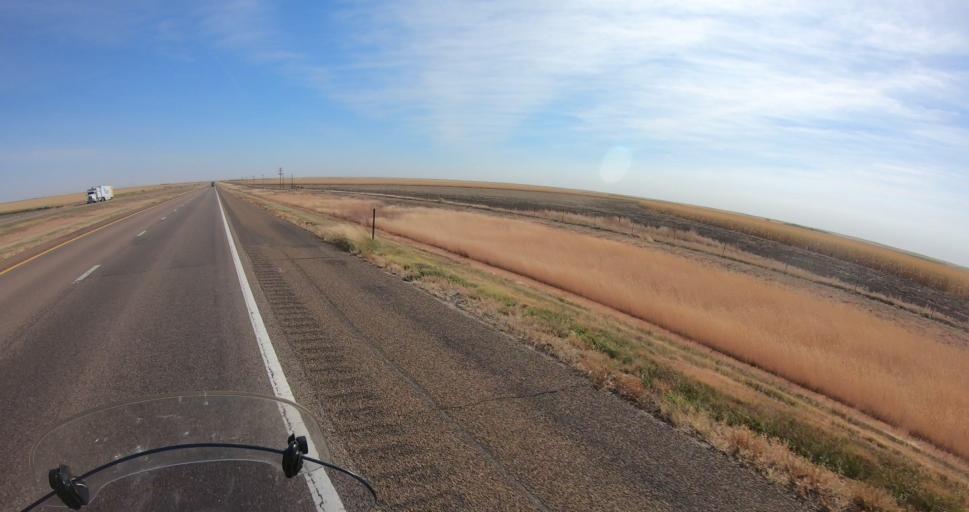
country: US
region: Kansas
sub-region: Sherman County
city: Goodland
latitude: 39.3299
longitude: -101.4596
